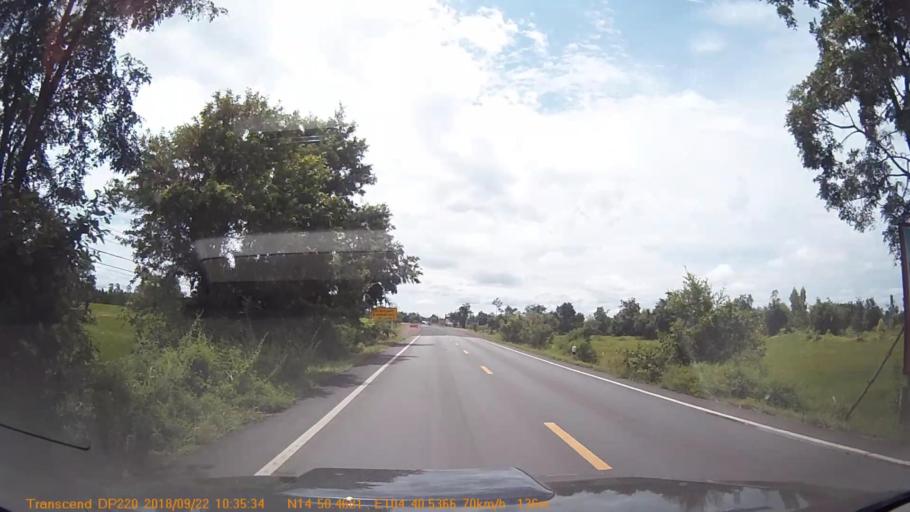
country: TH
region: Sisaket
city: Benchalak
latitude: 14.8412
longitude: 104.6756
